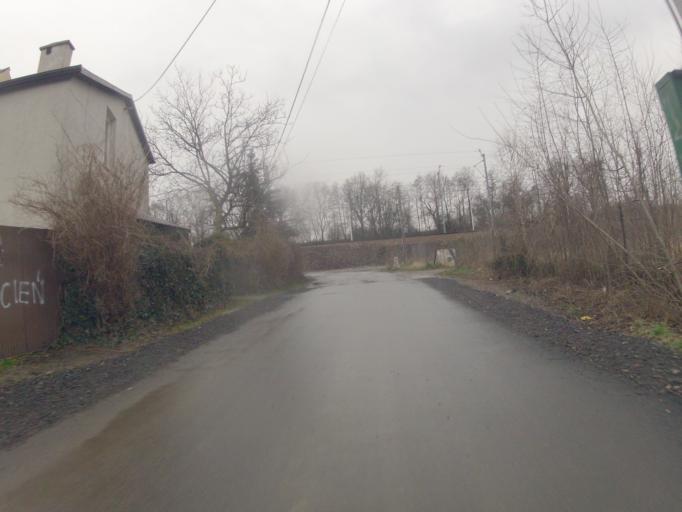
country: PL
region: Lesser Poland Voivodeship
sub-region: Powiat wielicki
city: Czarnochowice
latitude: 50.0188
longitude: 20.0509
